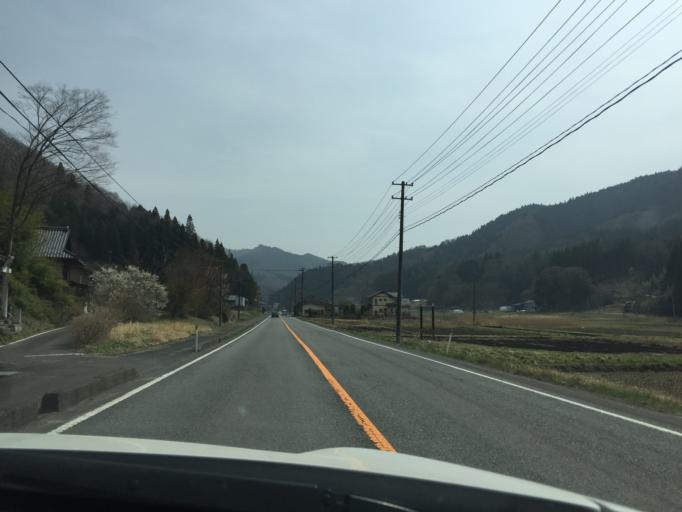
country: JP
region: Fukushima
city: Ishikawa
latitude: 37.0907
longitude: 140.5152
